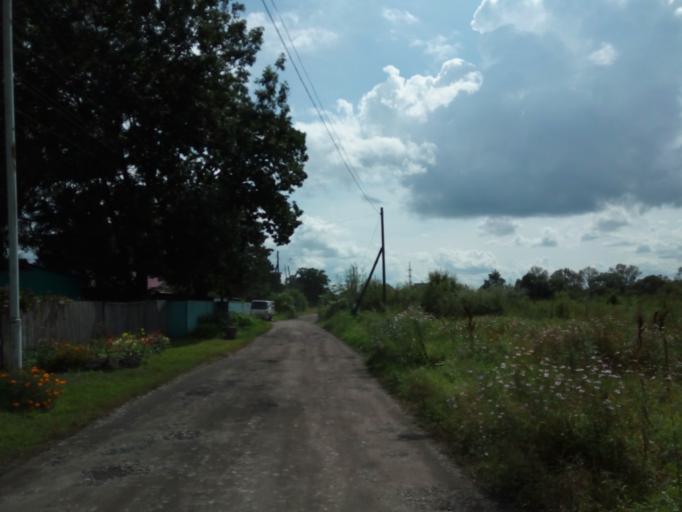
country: RU
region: Primorskiy
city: Dal'nerechensk
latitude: 45.9515
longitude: 133.8165
